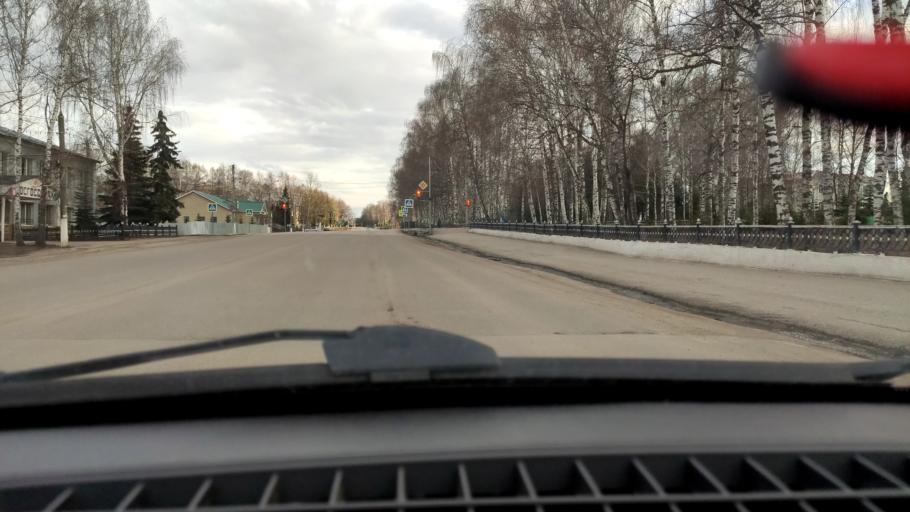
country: RU
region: Bashkortostan
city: Tolbazy
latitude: 54.0169
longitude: 55.8864
